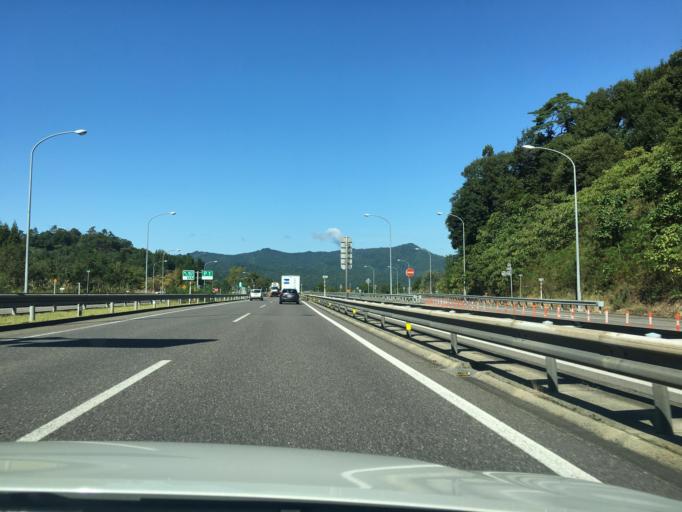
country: JP
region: Fukushima
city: Kitakata
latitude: 37.5733
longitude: 139.6529
